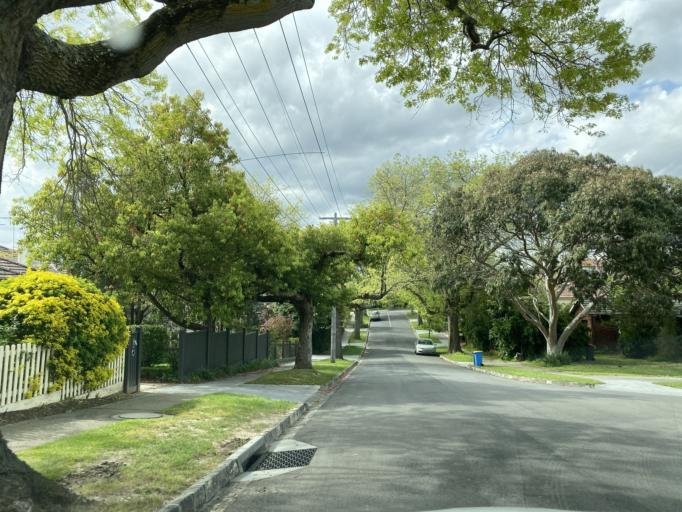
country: AU
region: Victoria
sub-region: Boroondara
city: Ashburton
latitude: -37.8458
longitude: 145.0932
